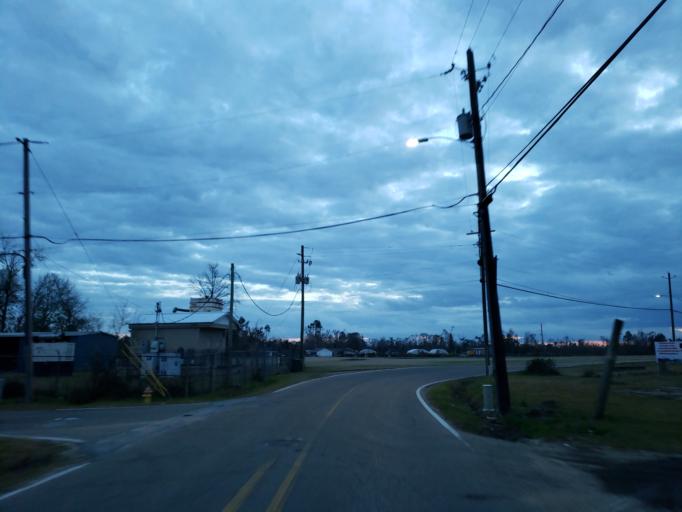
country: US
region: Mississippi
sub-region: Forrest County
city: Petal
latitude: 31.3327
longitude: -89.2603
